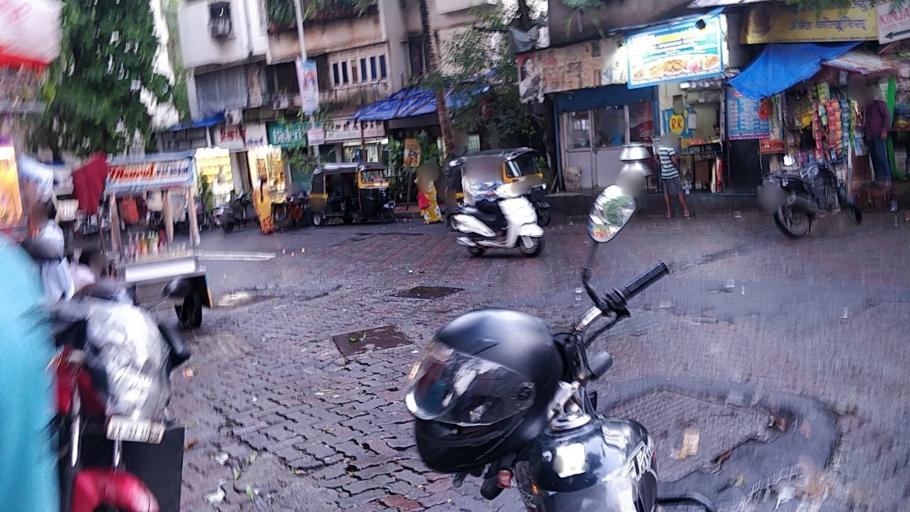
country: IN
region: Maharashtra
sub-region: Mumbai Suburban
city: Mumbai
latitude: 19.1120
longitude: 72.8490
